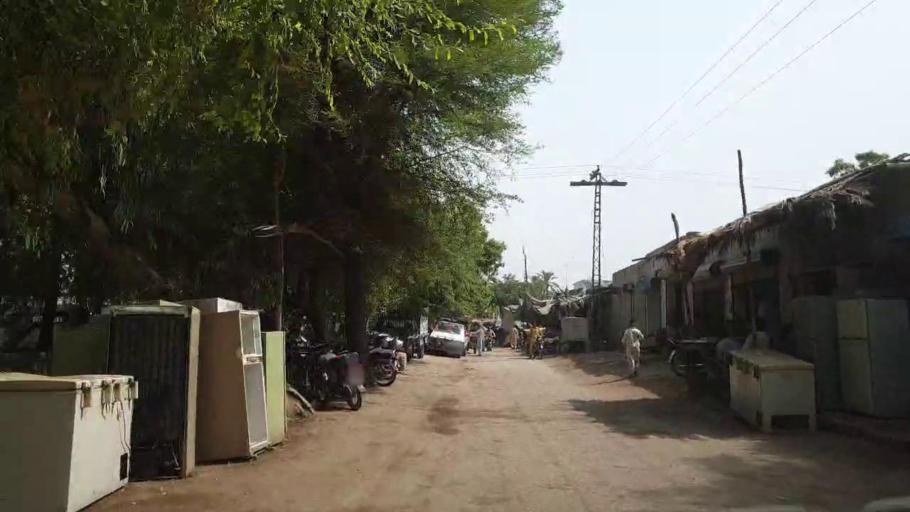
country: PK
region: Sindh
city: Gambat
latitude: 27.3834
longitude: 68.5160
